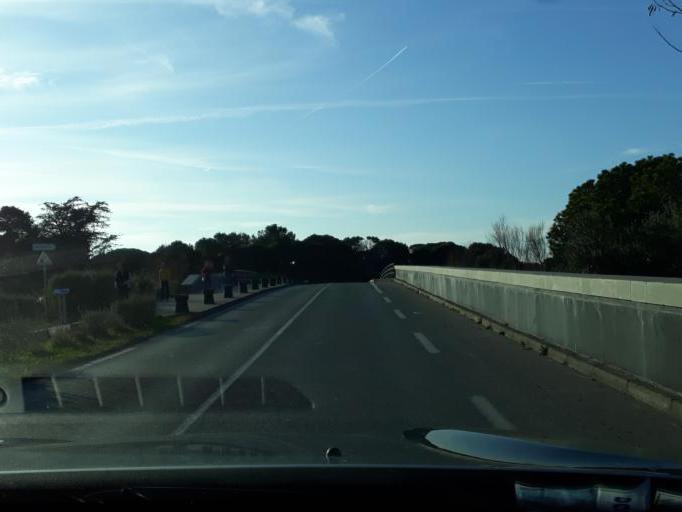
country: FR
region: Languedoc-Roussillon
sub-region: Departement de l'Herault
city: Marseillan
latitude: 43.3213
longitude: 3.5324
